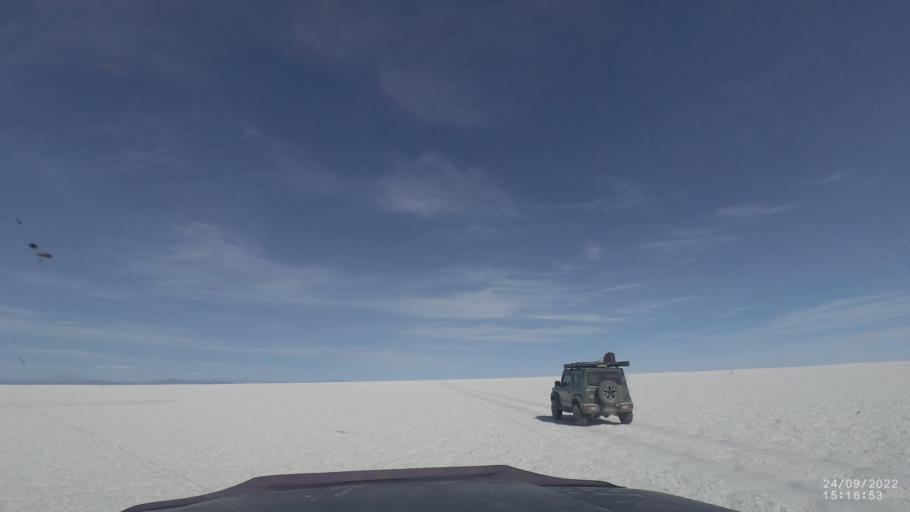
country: BO
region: Potosi
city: Colchani
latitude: -19.9851
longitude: -67.4320
